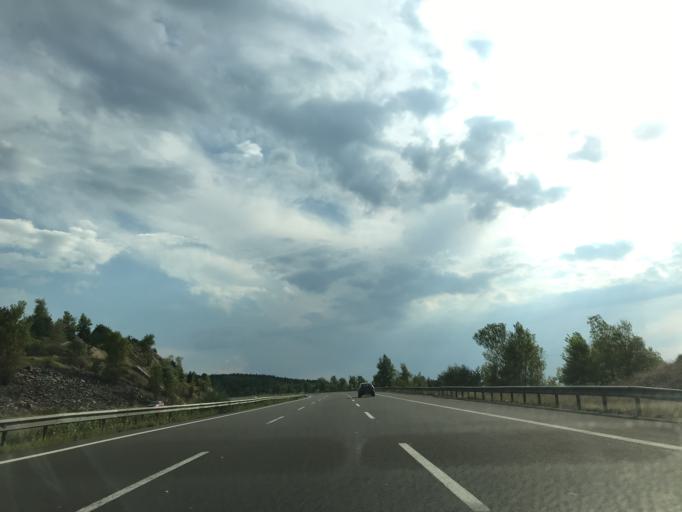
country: TR
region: Bolu
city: Gerede
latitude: 40.6495
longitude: 32.2349
